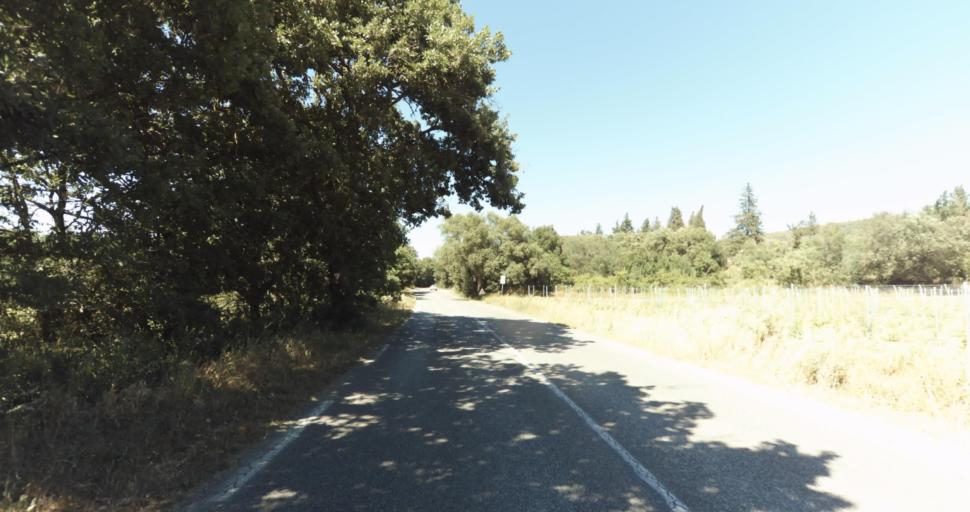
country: FR
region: Provence-Alpes-Cote d'Azur
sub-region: Departement du Var
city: Gassin
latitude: 43.2257
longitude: 6.5717
